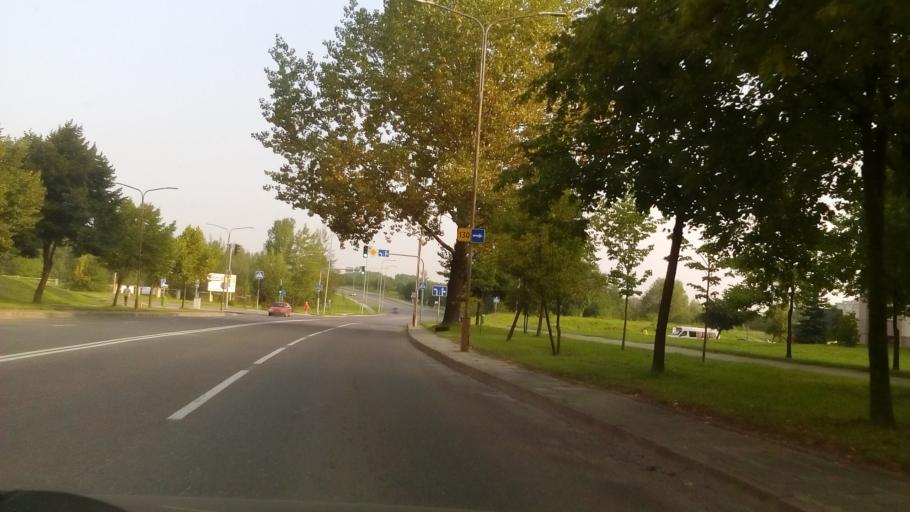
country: LT
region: Alytaus apskritis
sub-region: Alytus
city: Alytus
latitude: 54.3985
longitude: 24.0154
